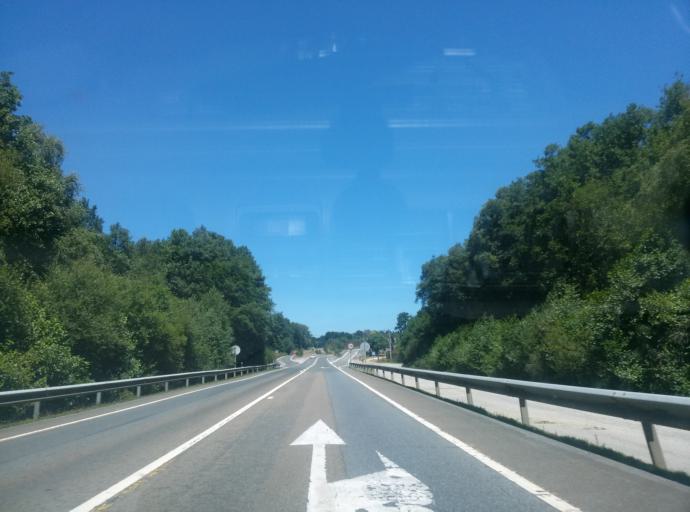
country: ES
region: Galicia
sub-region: Provincia de Lugo
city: Mos
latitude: 43.0899
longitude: -7.4788
